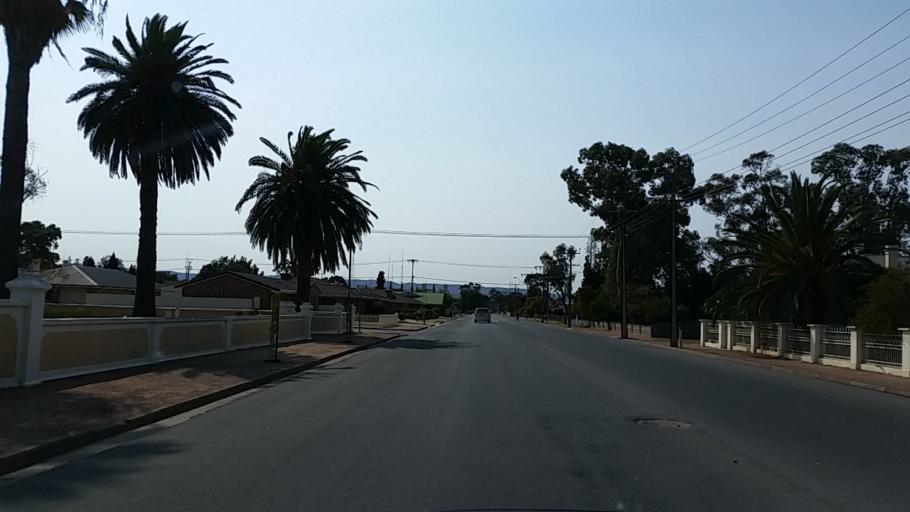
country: AU
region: South Australia
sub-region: Port Pirie City and Dists
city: Port Pirie
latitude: -33.1813
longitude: 137.9959
